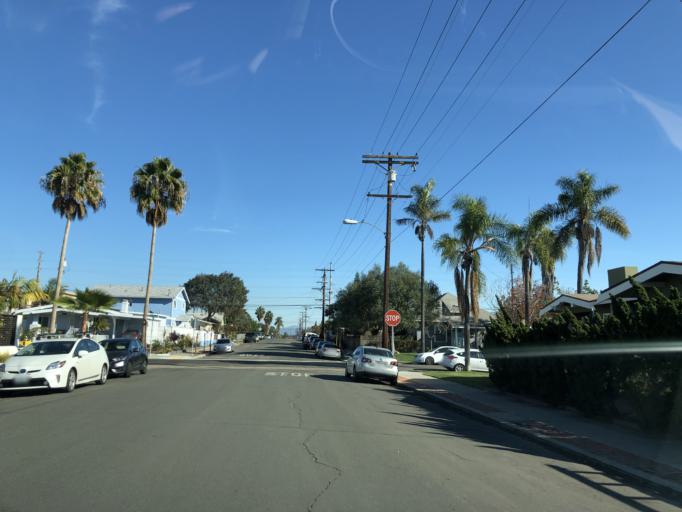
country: US
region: California
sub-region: San Diego County
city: San Diego
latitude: 32.7420
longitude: -117.1266
